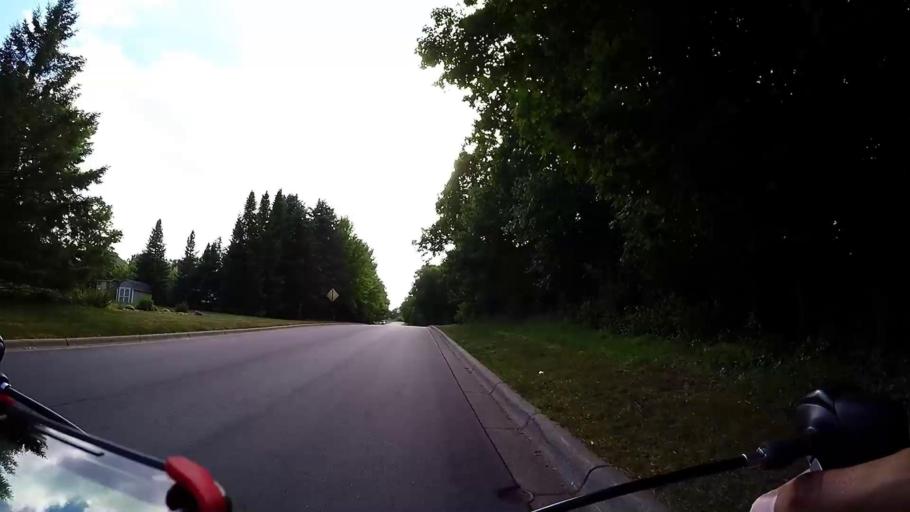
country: US
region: Minnesota
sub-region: Hennepin County
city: Eden Prairie
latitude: 44.8837
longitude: -93.4630
